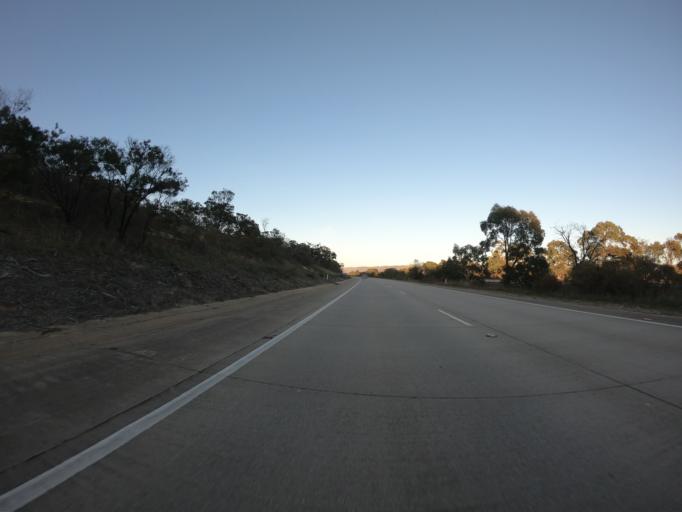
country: AU
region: New South Wales
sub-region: Yass Valley
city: Gundaroo
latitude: -34.9083
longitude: 149.4473
